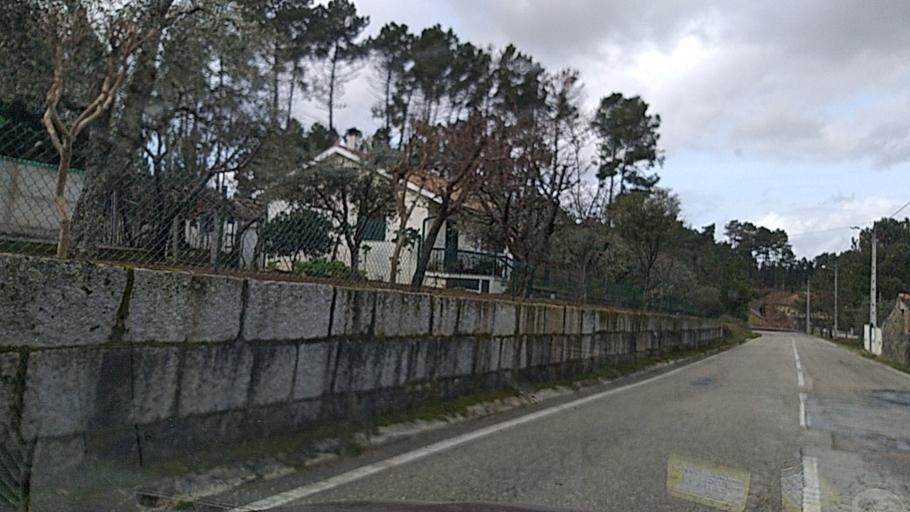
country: PT
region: Viseu
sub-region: Satao
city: Satao
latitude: 40.6574
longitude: -7.6611
